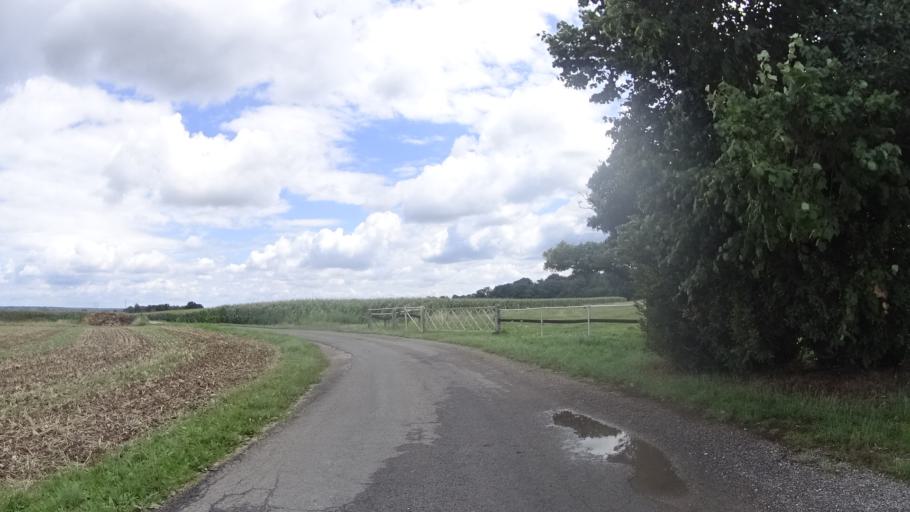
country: FR
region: Champagne-Ardenne
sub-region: Departement de la Haute-Marne
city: Montier-en-Der
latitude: 48.4932
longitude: 4.7642
